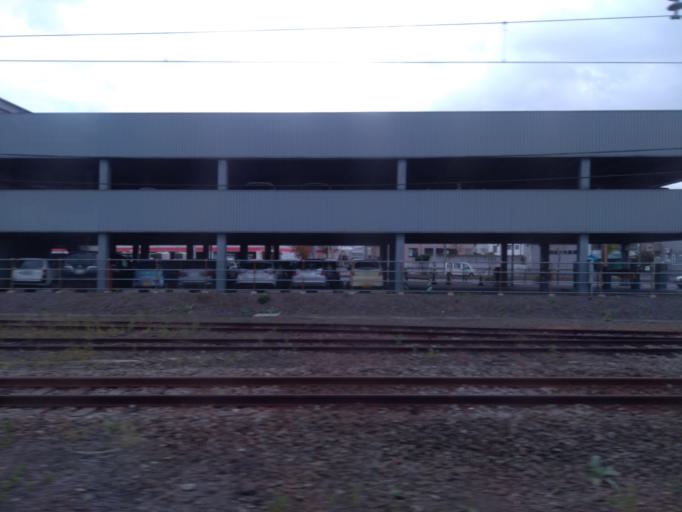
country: JP
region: Hokkaido
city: Hakodate
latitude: 41.8024
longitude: 140.7339
